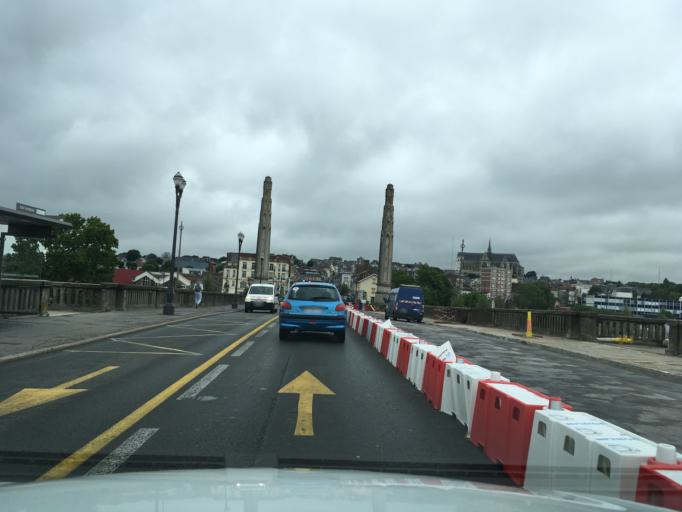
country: FR
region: Picardie
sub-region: Departement de l'Aisne
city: Harly
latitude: 49.8404
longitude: 3.2983
